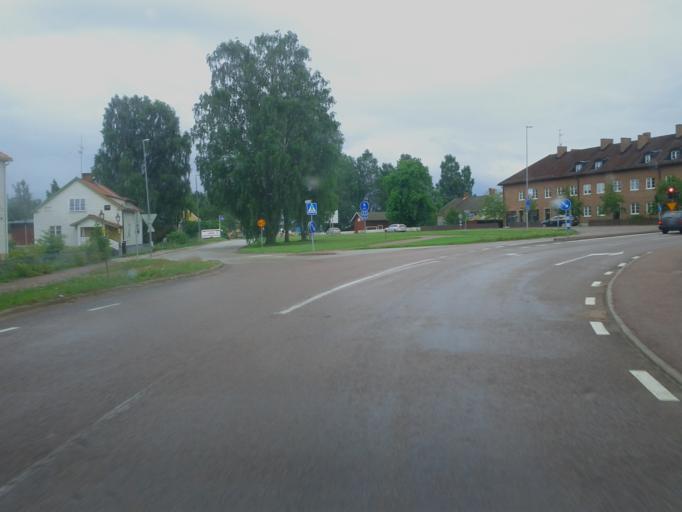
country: SE
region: Dalarna
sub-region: Mora Kommun
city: Mora
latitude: 61.0100
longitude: 14.5505
